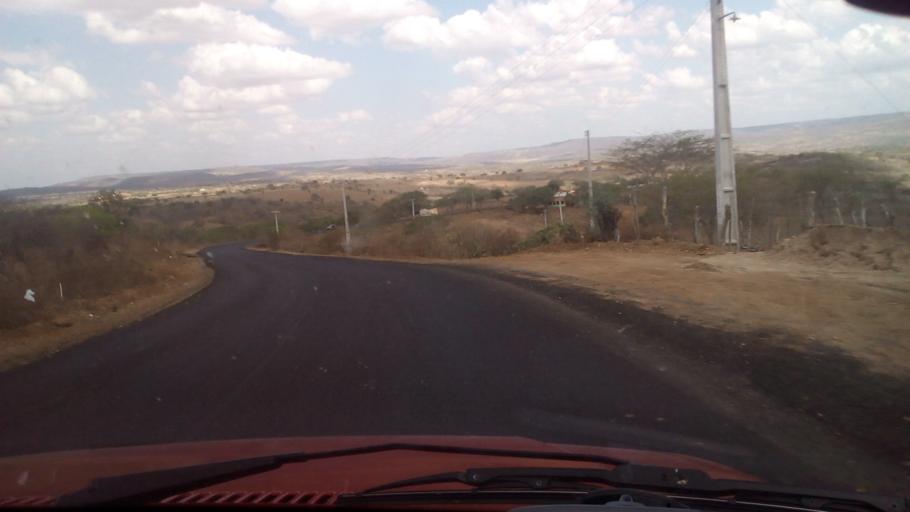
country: BR
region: Paraiba
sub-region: Cacimba De Dentro
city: Cacimba de Dentro
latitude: -6.6572
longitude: -35.7689
